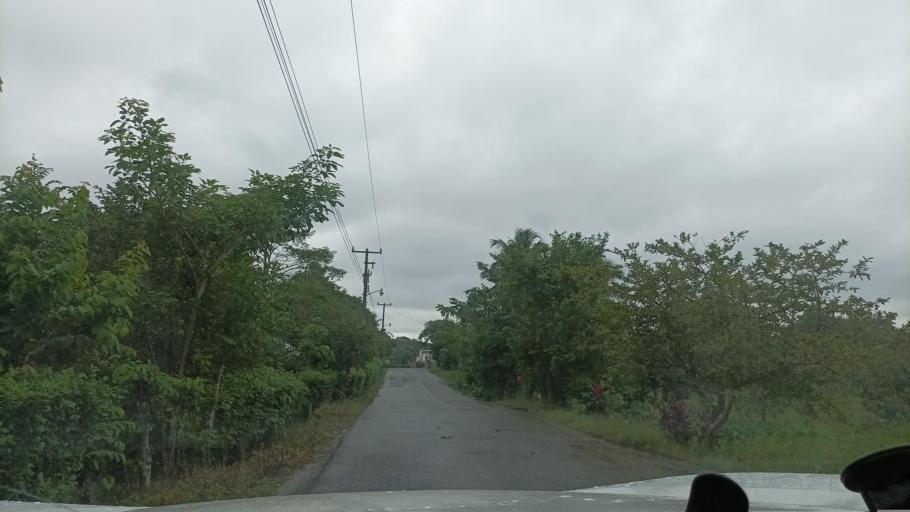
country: MX
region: Veracruz
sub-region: Moloacan
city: Cuichapa
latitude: 17.7617
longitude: -94.3913
